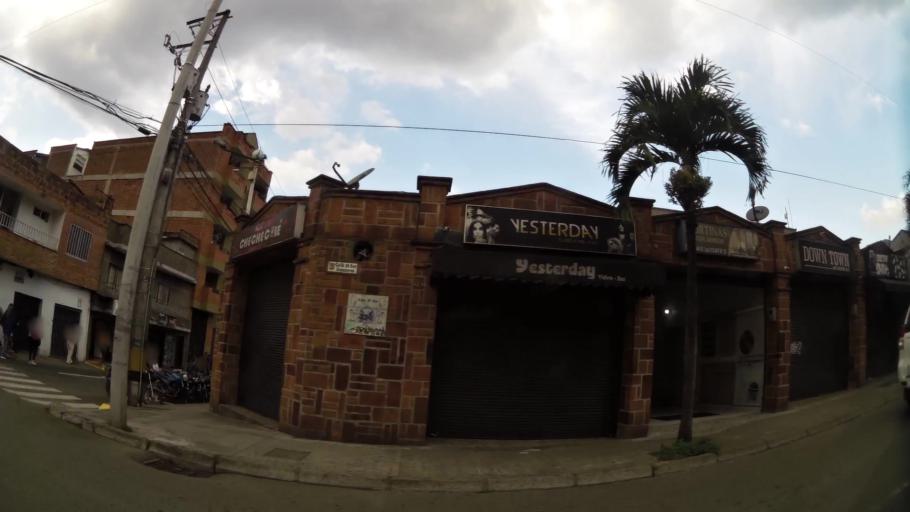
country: CO
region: Antioquia
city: Envigado
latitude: 6.1686
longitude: -75.5886
